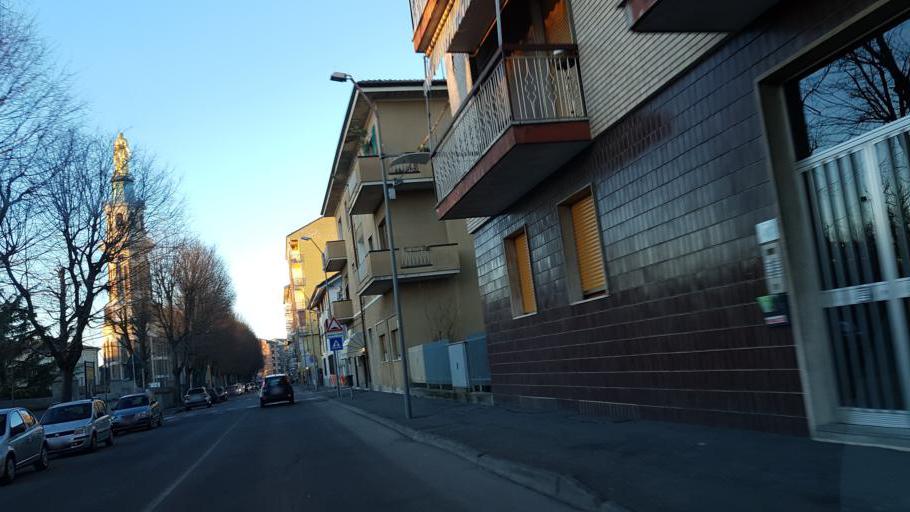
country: IT
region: Piedmont
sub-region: Provincia di Alessandria
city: Tortona
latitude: 44.8861
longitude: 8.8591
